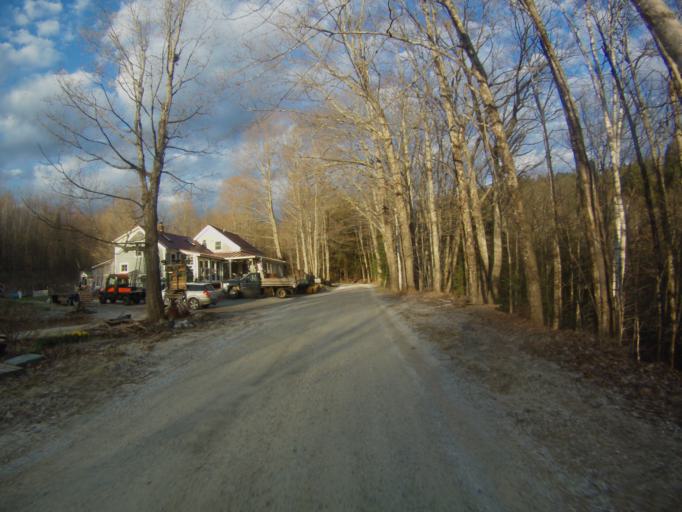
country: US
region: Vermont
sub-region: Rutland County
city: Brandon
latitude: 43.8473
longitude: -73.0273
